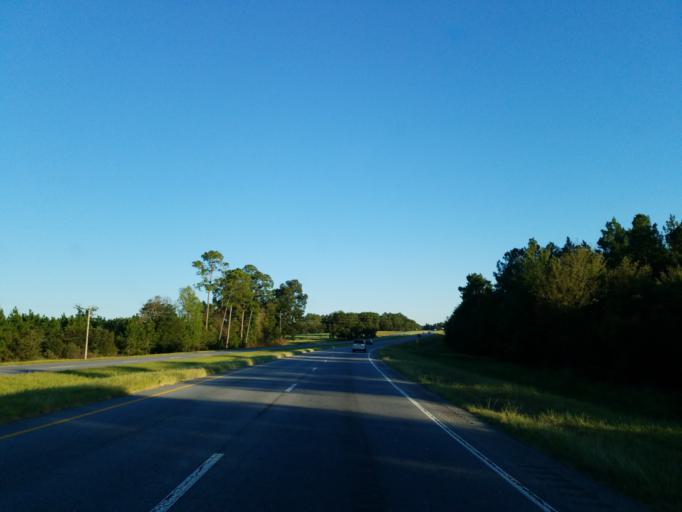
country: US
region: Georgia
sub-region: Worth County
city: Sylvester
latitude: 31.4956
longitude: -83.7089
